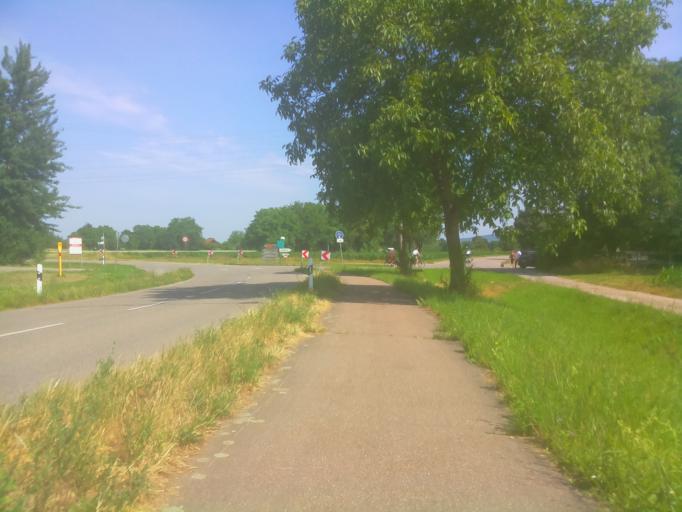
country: DE
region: Baden-Wuerttemberg
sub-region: Karlsruhe Region
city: Weinheim
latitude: 49.5577
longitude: 8.6449
